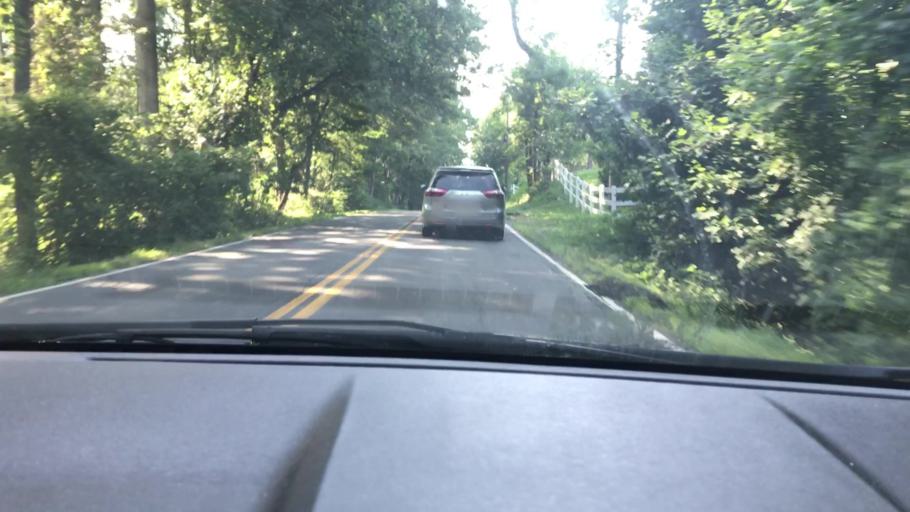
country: US
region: Virginia
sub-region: Fairfax County
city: Great Falls
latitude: 38.9727
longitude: -77.2523
